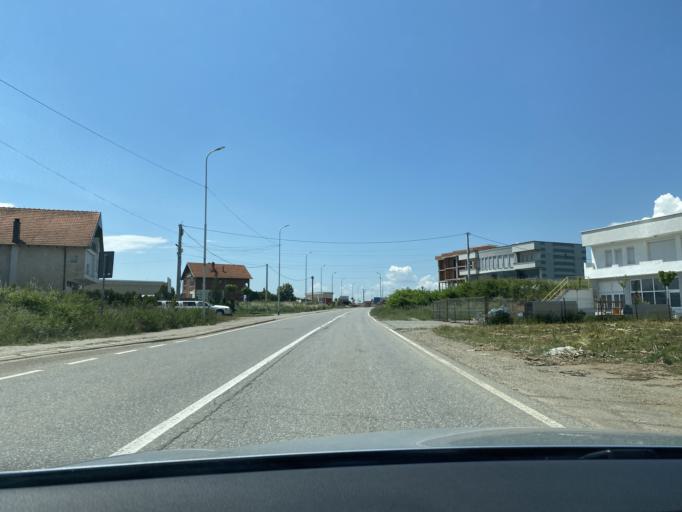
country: XK
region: Pristina
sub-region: Podujevo
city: Podujeva
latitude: 42.9043
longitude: 21.2143
